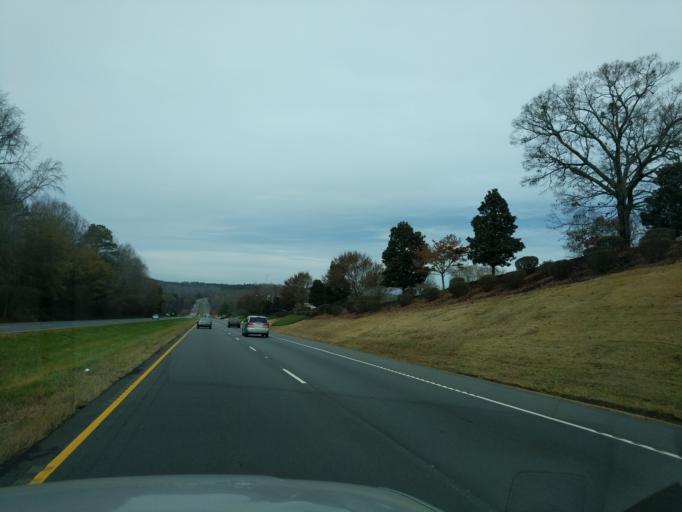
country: US
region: South Carolina
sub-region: Anderson County
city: Pendleton
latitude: 34.6407
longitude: -82.7911
